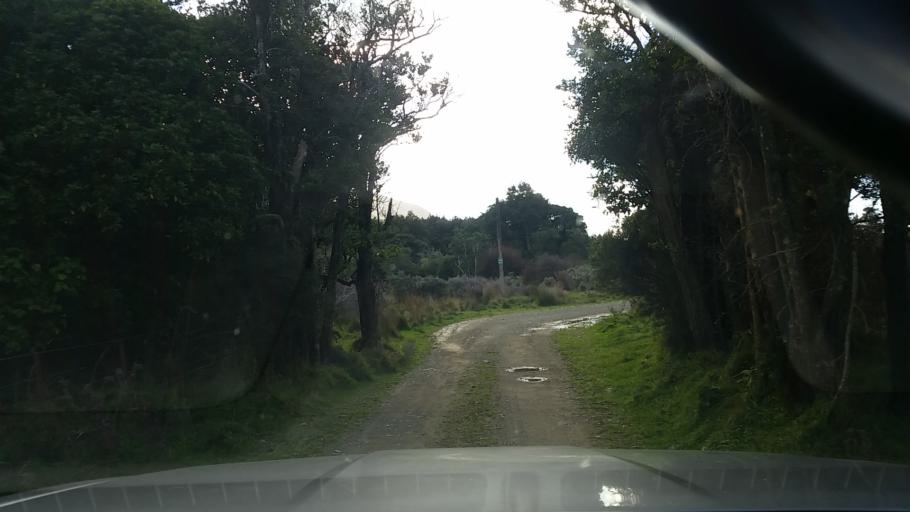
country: NZ
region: Marlborough
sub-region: Marlborough District
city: Picton
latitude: -41.0555
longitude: 174.1094
